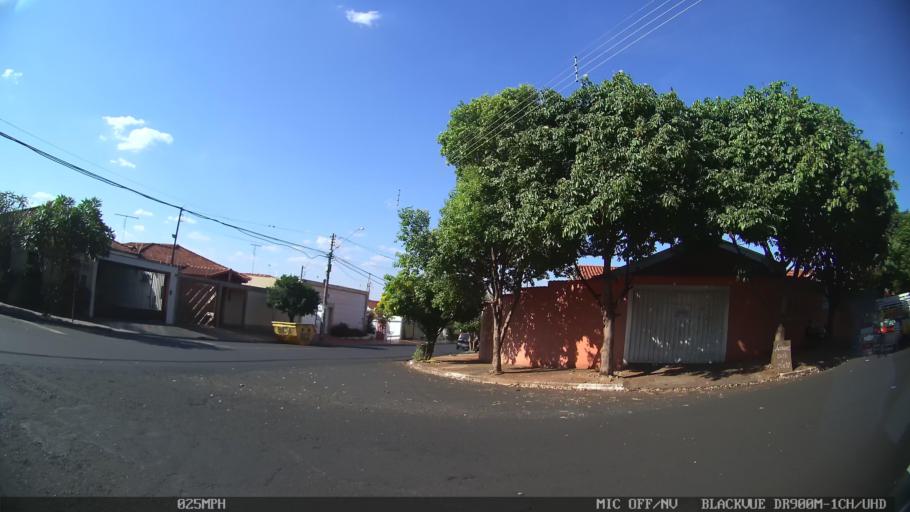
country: BR
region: Sao Paulo
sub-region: Ribeirao Preto
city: Ribeirao Preto
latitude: -21.1752
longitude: -47.7699
